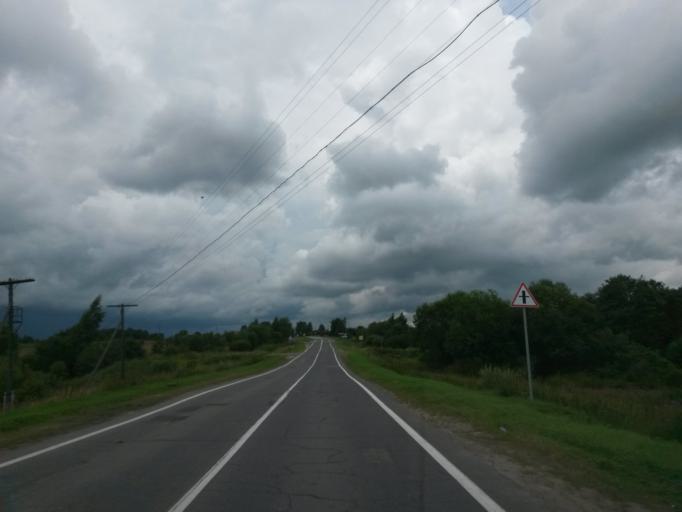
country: RU
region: Jaroslavl
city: Konstantinovskiy
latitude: 57.8416
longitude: 39.6506
